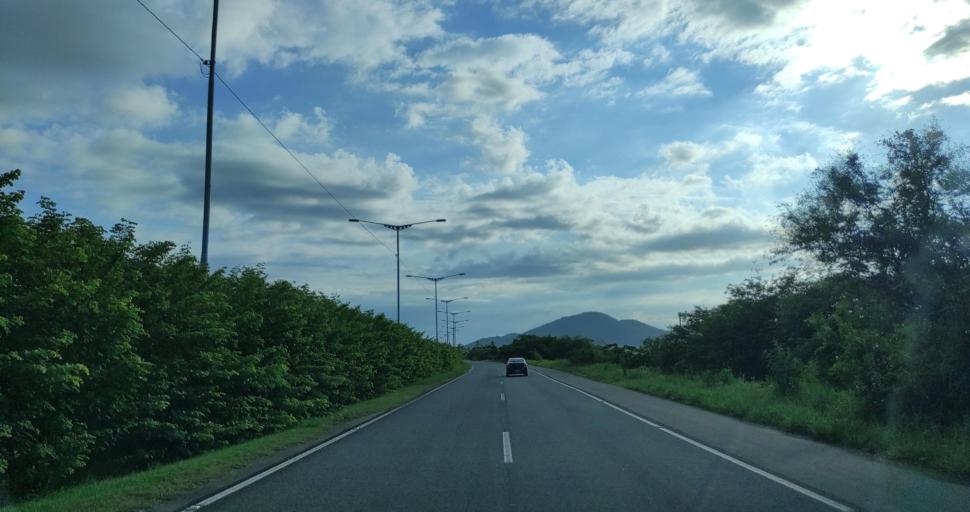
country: BR
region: Santa Catarina
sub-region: Penha
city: Penha
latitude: -26.8036
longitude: -48.6334
